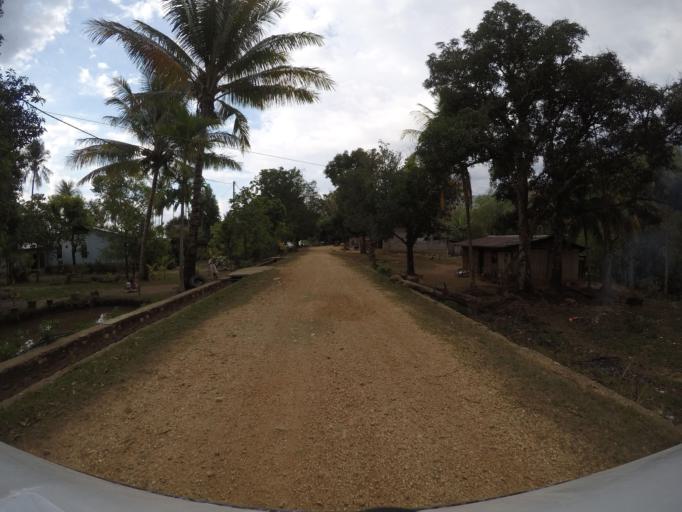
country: TL
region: Bobonaro
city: Maliana
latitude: -8.9610
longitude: 125.2180
